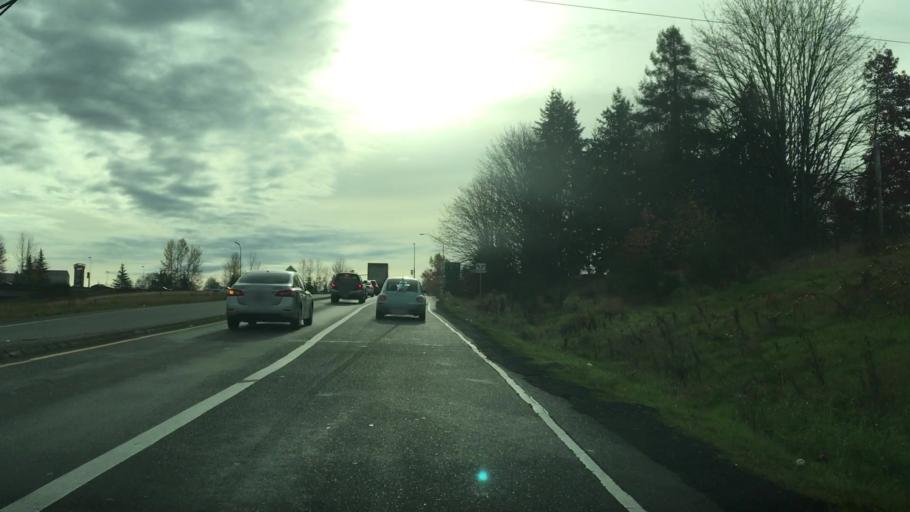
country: US
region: Washington
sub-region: Pierce County
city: Puyallup
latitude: 47.1634
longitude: -122.2980
